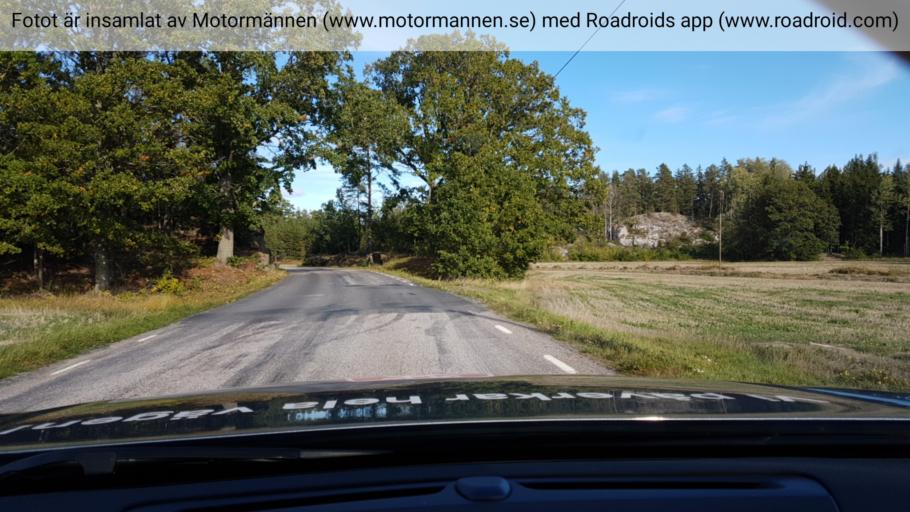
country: SE
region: OEstergoetland
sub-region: Valdemarsviks Kommun
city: Valdemarsvik
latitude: 58.0529
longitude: 16.6164
